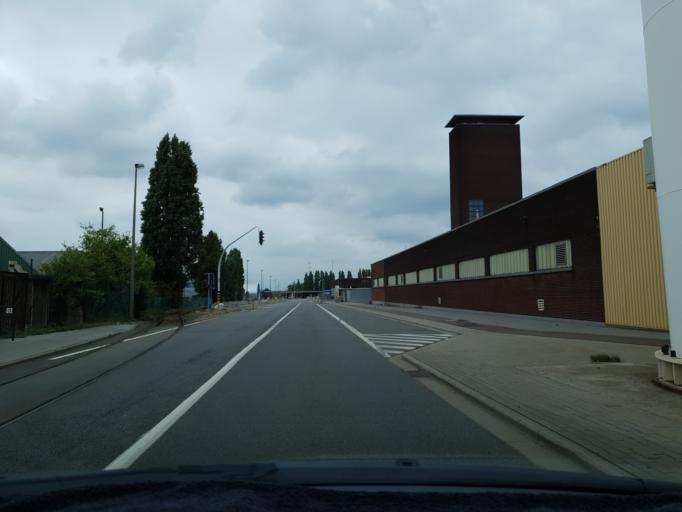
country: BE
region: Flanders
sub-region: Provincie Antwerpen
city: Antwerpen
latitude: 51.2613
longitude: 4.3834
